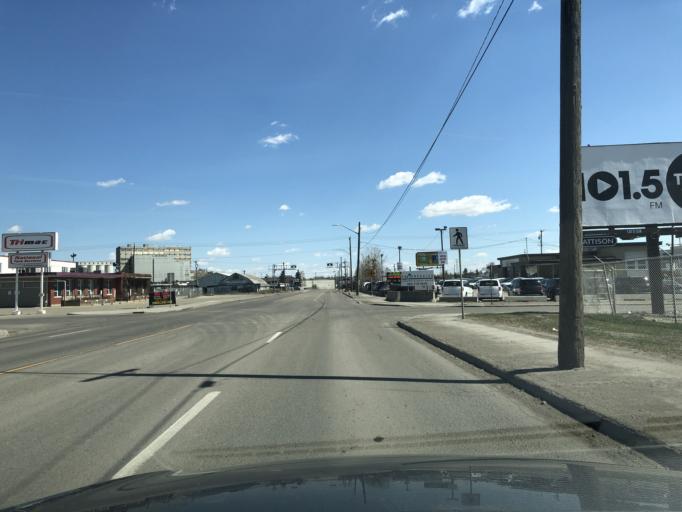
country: CA
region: Alberta
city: Calgary
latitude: 51.0186
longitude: -114.0272
